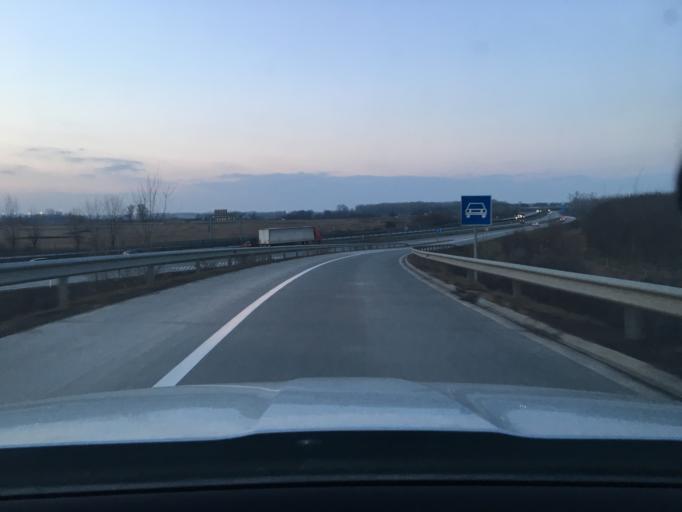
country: HU
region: Pest
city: Vecses
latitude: 47.4060
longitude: 19.3172
